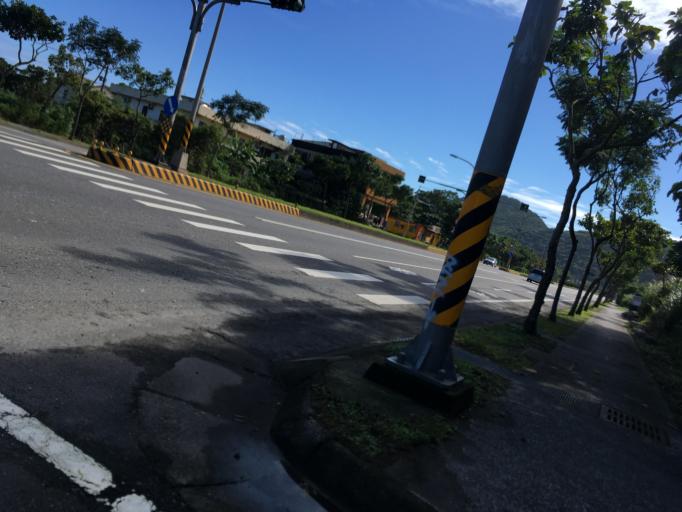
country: TW
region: Taiwan
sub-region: Yilan
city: Yilan
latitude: 24.6132
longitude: 121.8510
